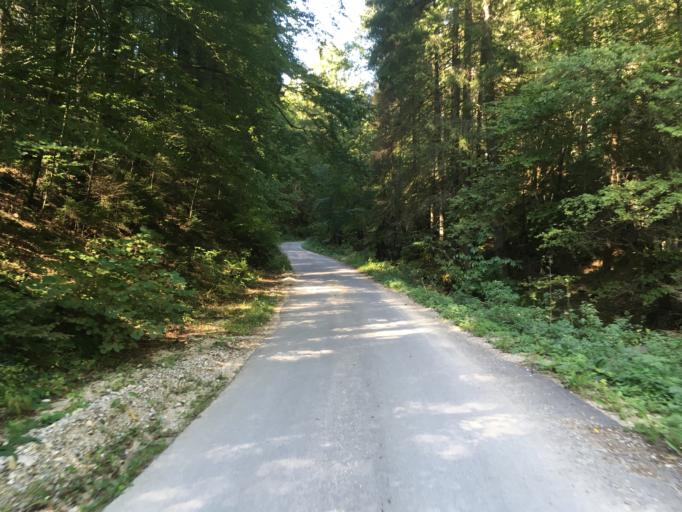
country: SK
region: Trenciansky
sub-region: Okres Povazska Bystrica
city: Povazska Bystrica
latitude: 49.0034
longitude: 18.4694
